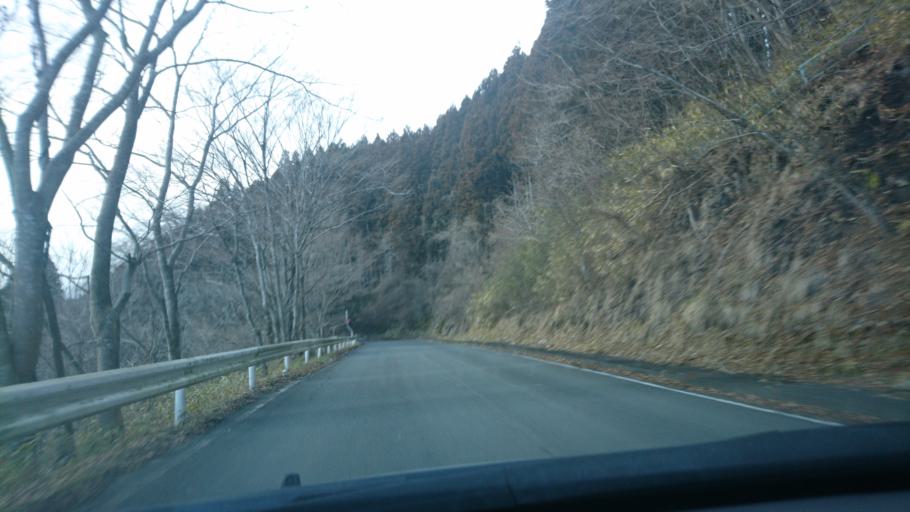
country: JP
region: Iwate
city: Ofunato
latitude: 38.9108
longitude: 141.5266
